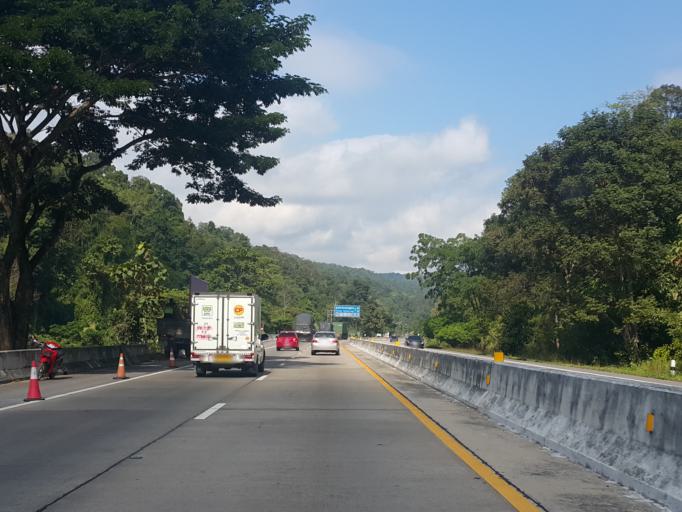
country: TH
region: Lamphun
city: Mae Tha
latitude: 18.3825
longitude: 99.2220
